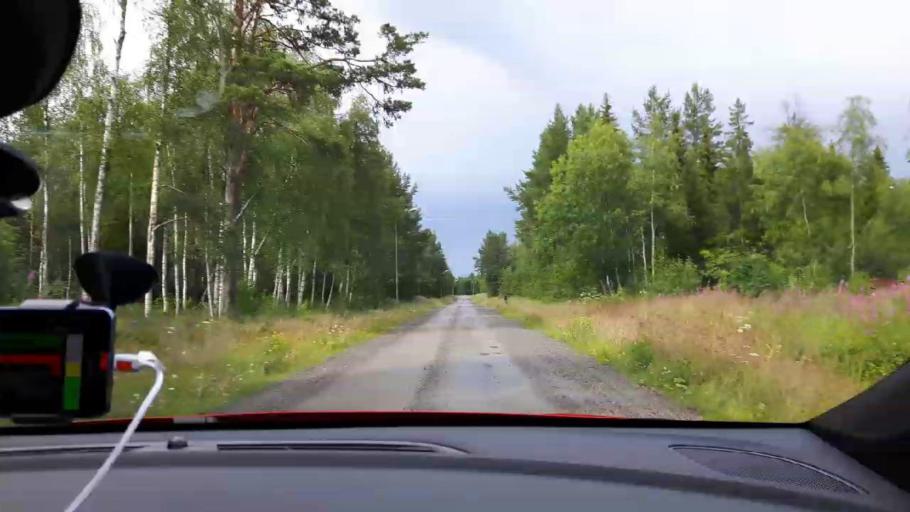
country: SE
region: Jaemtland
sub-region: Stroemsunds Kommun
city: Stroemsund
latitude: 64.0552
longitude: 15.8927
